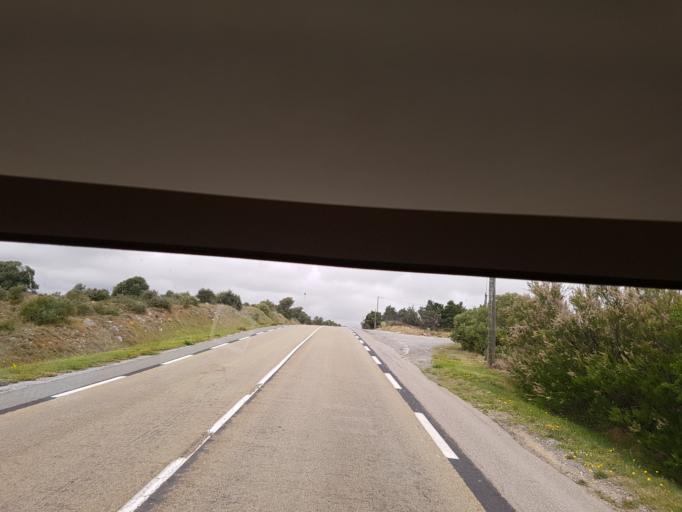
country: FR
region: Languedoc-Roussillon
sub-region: Departement de l'Aude
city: Leucate
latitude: 42.9048
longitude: 3.0005
